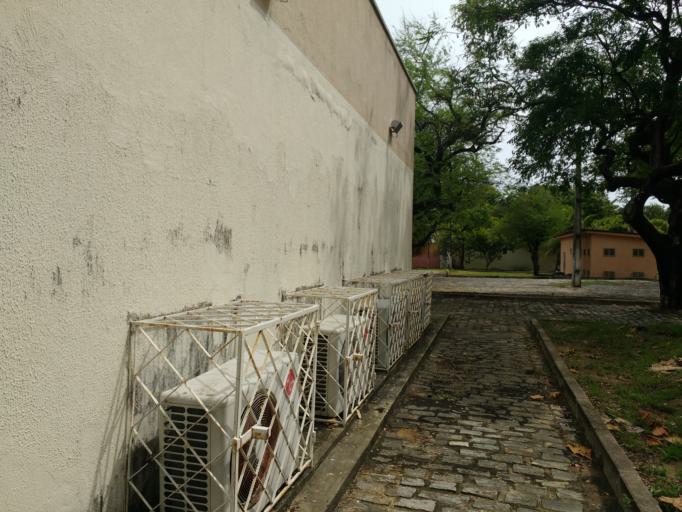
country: BR
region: Ceara
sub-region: Fortaleza
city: Fortaleza
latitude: -3.7477
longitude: -38.5767
